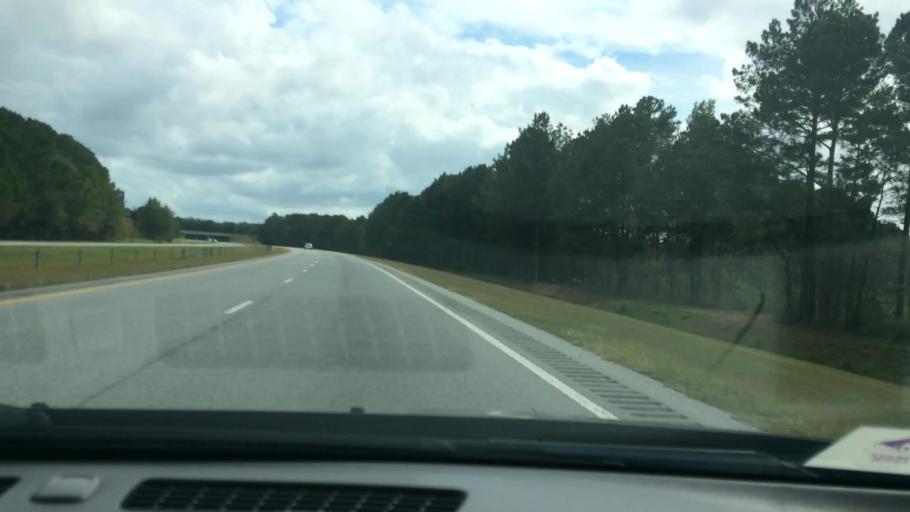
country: US
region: North Carolina
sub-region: Pitt County
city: Farmville
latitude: 35.6269
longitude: -77.7137
